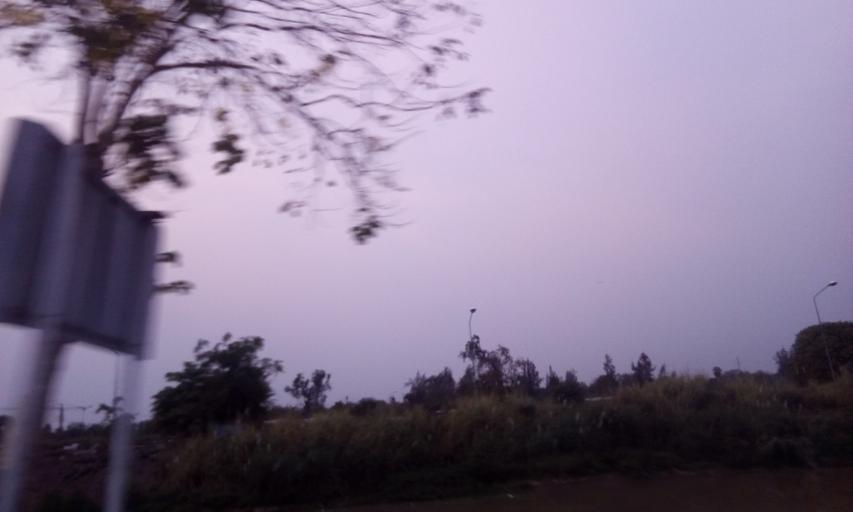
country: TH
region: Pathum Thani
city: Nong Suea
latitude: 14.0692
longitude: 100.8934
